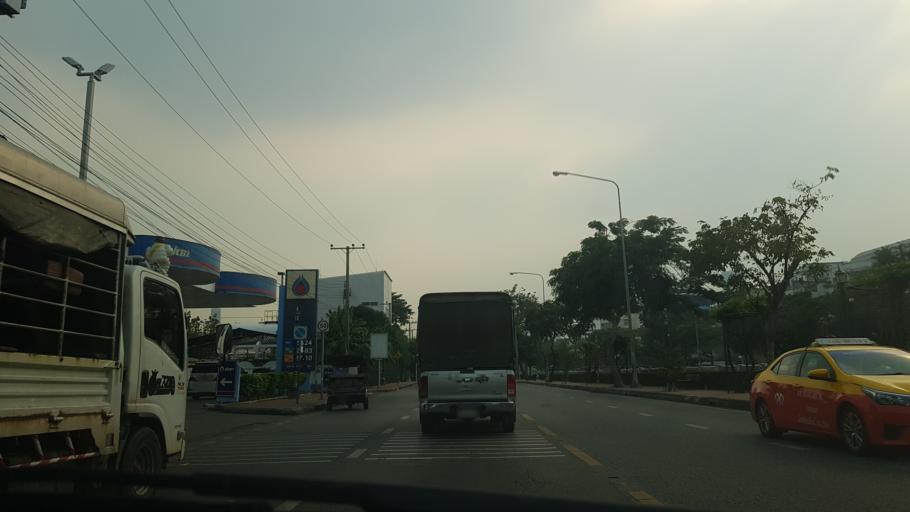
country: TH
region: Bangkok
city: Pathum Wan
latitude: 13.7433
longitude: 100.5162
